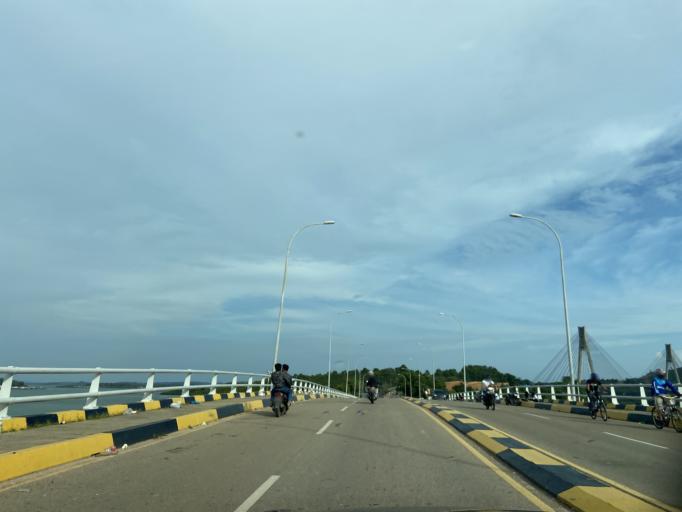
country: SG
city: Singapore
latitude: 0.9762
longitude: 104.0495
